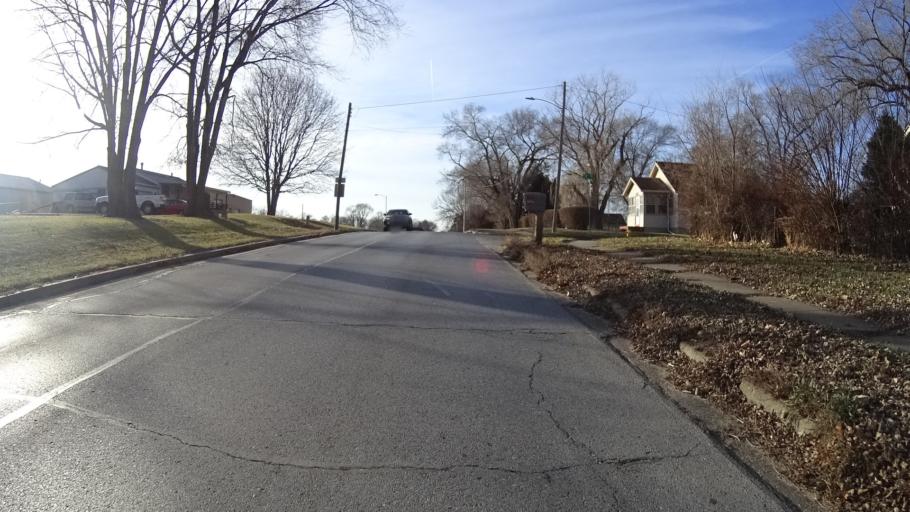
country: US
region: Nebraska
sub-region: Sarpy County
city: La Vista
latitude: 41.1909
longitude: -95.9646
